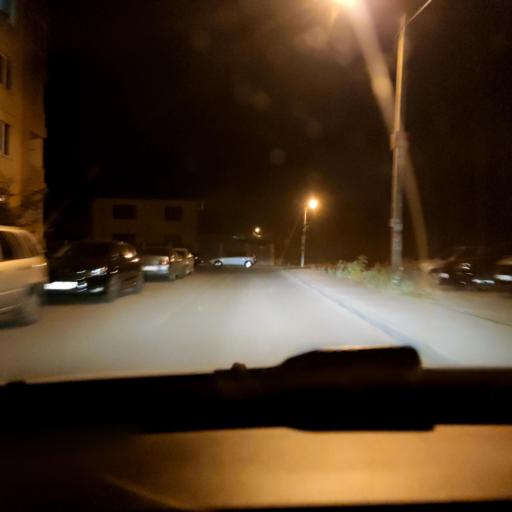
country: RU
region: Voronezj
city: Shilovo
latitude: 51.5643
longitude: 39.1175
